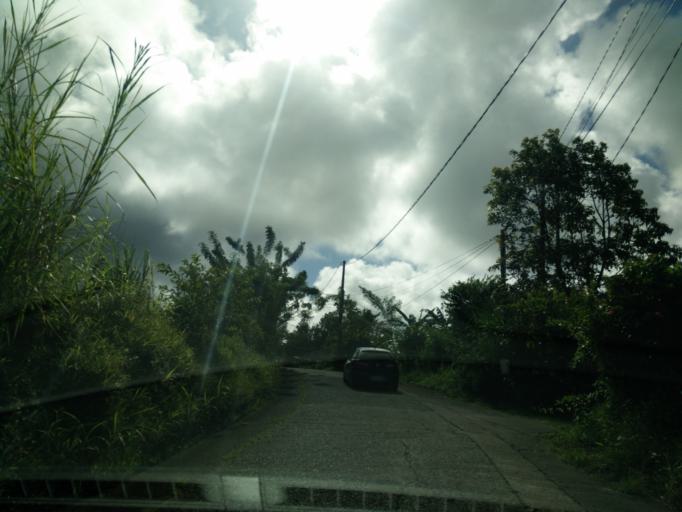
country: MQ
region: Martinique
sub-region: Martinique
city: Basse-Pointe
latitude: 14.8208
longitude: -61.1262
